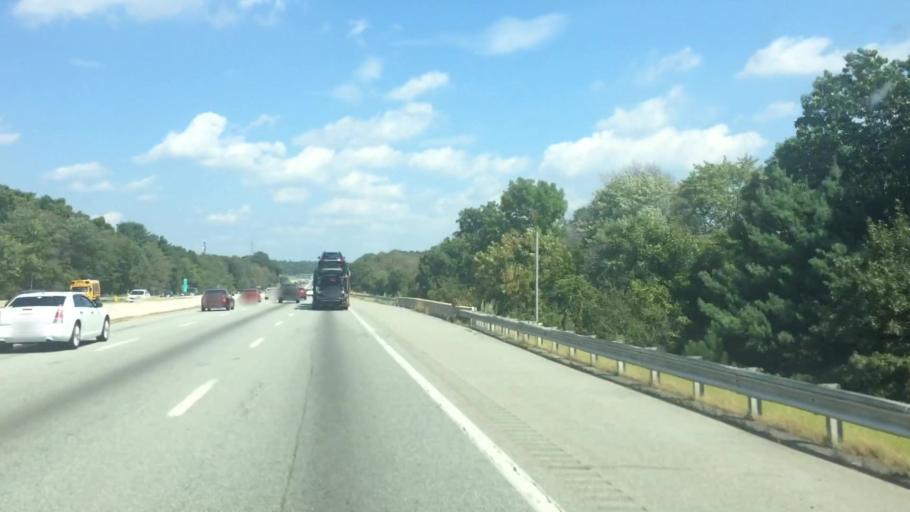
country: US
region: Massachusetts
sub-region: Middlesex County
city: Cochituate
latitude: 42.3279
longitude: -71.3293
